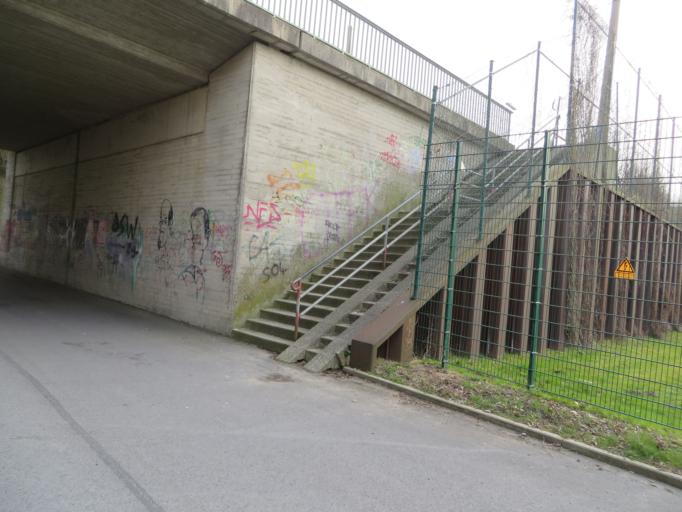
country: DE
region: North Rhine-Westphalia
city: Witten
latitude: 51.4475
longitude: 7.3575
